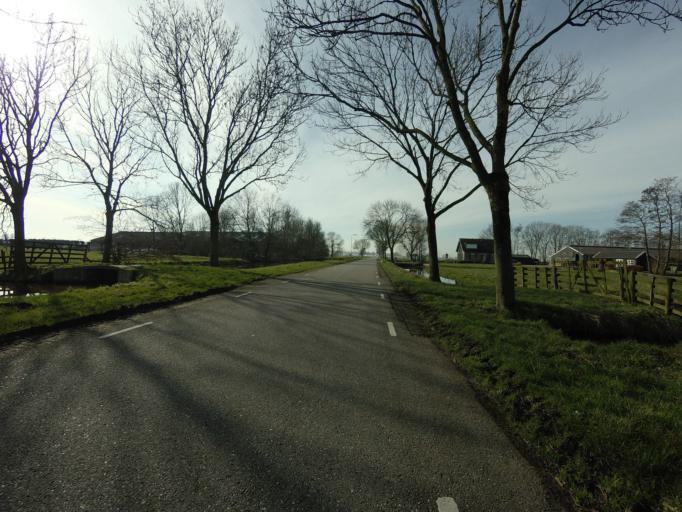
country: NL
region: South Holland
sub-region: Gemeente Hardinxveld-Giessendam
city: Neder-Hardinxveld
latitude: 51.8616
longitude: 4.8127
